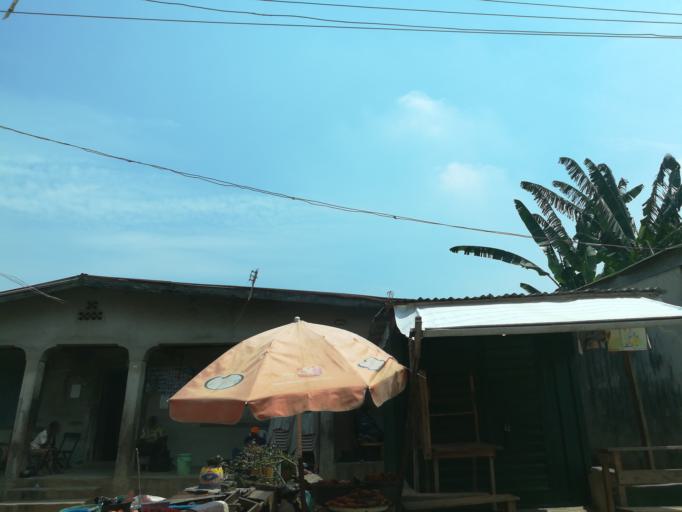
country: NG
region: Lagos
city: Ikorodu
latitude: 6.6217
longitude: 3.4930
